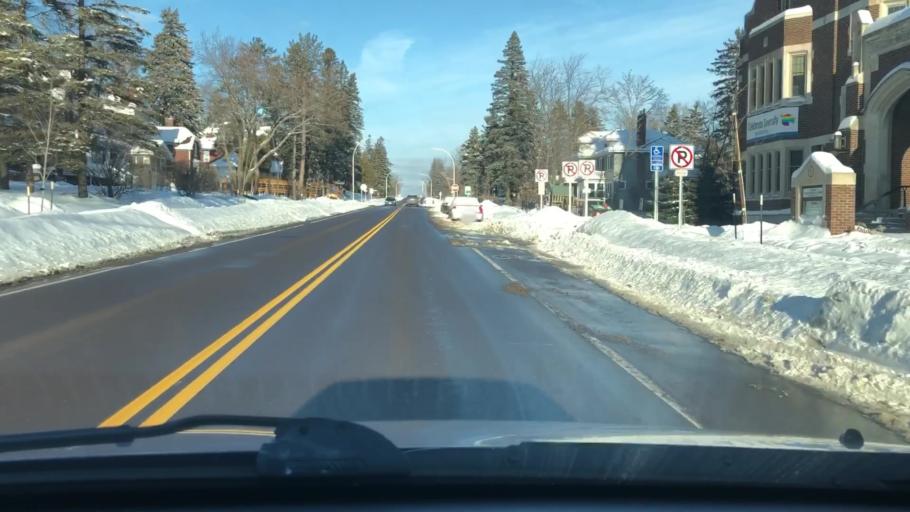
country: US
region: Minnesota
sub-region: Saint Louis County
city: Duluth
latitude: 46.8117
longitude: -92.0737
